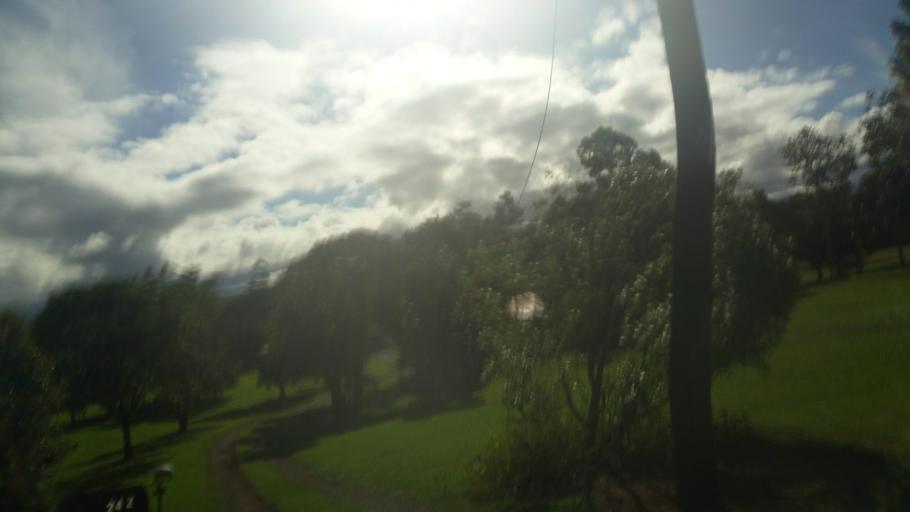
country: AU
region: Queensland
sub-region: Cassowary Coast
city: Innisfail
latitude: -17.5301
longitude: 145.9794
